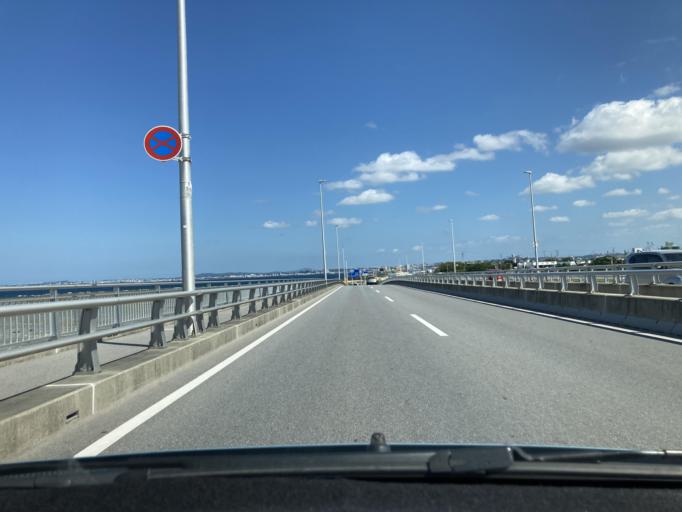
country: JP
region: Okinawa
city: Ginowan
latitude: 26.2699
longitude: 127.7048
